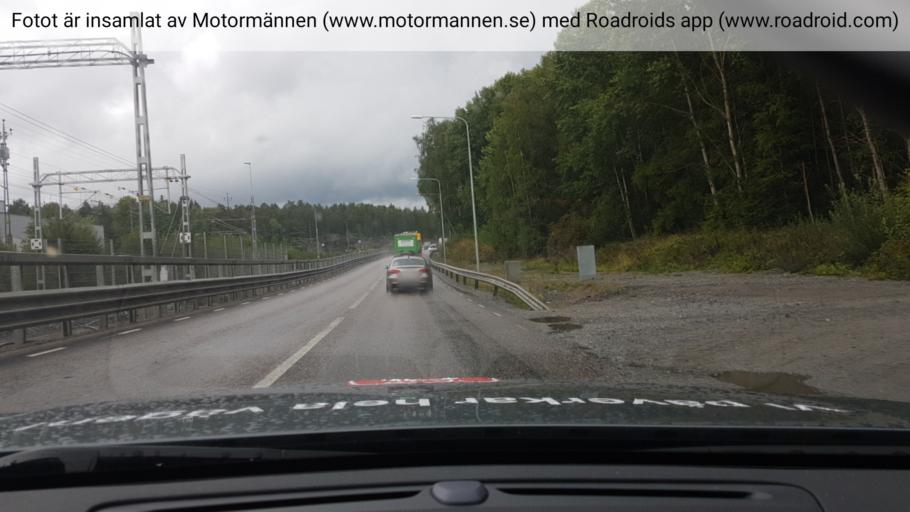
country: SE
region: Stockholm
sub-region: Botkyrka Kommun
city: Tullinge
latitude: 59.2159
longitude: 17.9419
